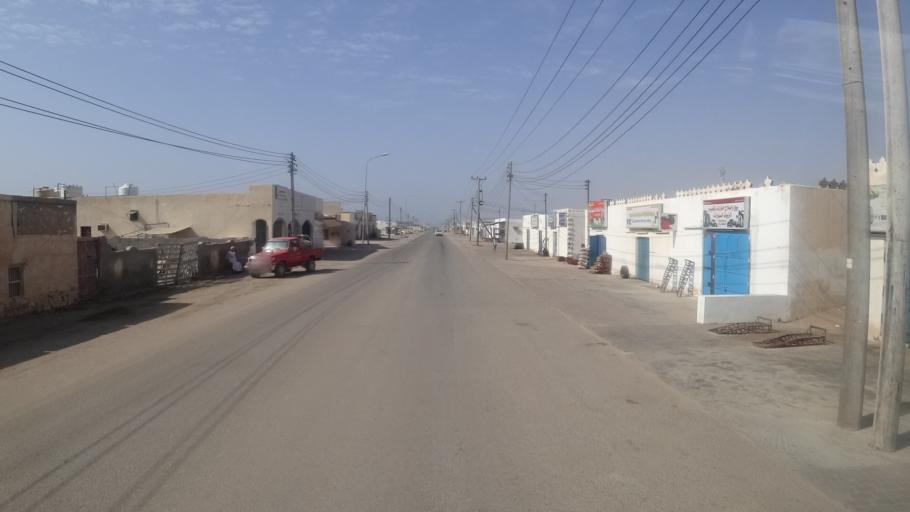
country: OM
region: Ash Sharqiyah
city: Sur
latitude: 22.1792
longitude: 59.7621
